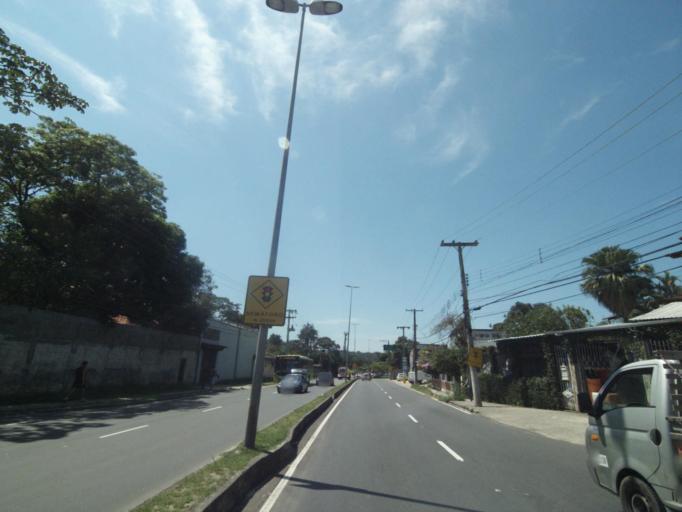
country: BR
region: Rio de Janeiro
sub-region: Sao Goncalo
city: Sao Goncalo
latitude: -22.8800
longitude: -43.0274
